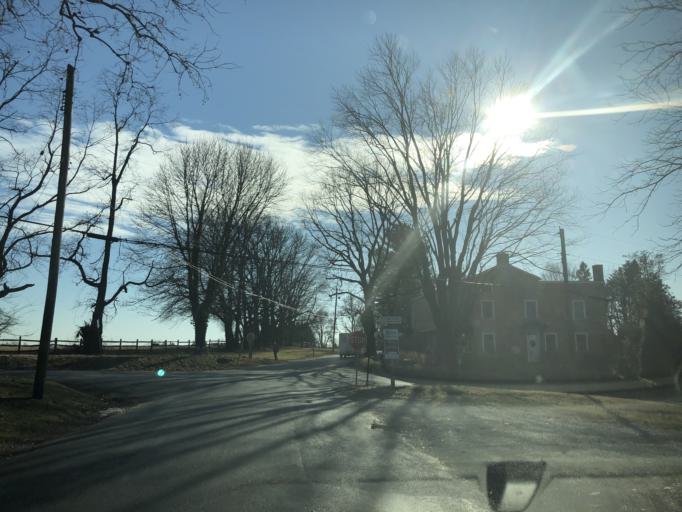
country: US
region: Pennsylvania
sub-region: Chester County
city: Upland
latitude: 39.8869
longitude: -75.7743
